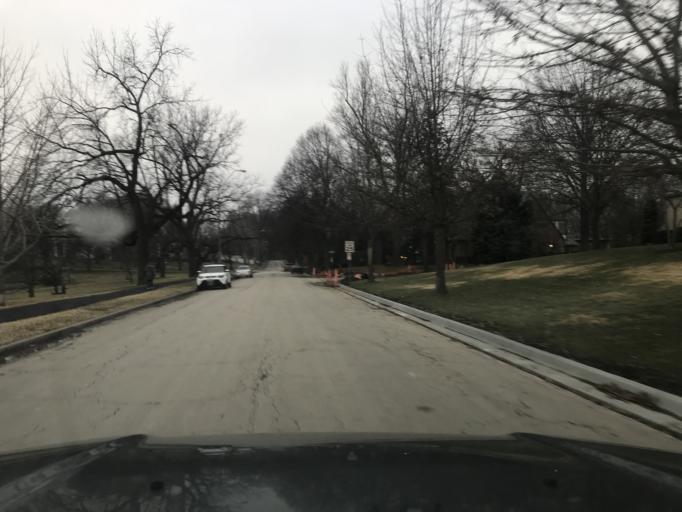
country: US
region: Kansas
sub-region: Johnson County
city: Westwood
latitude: 39.0295
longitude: -94.5971
